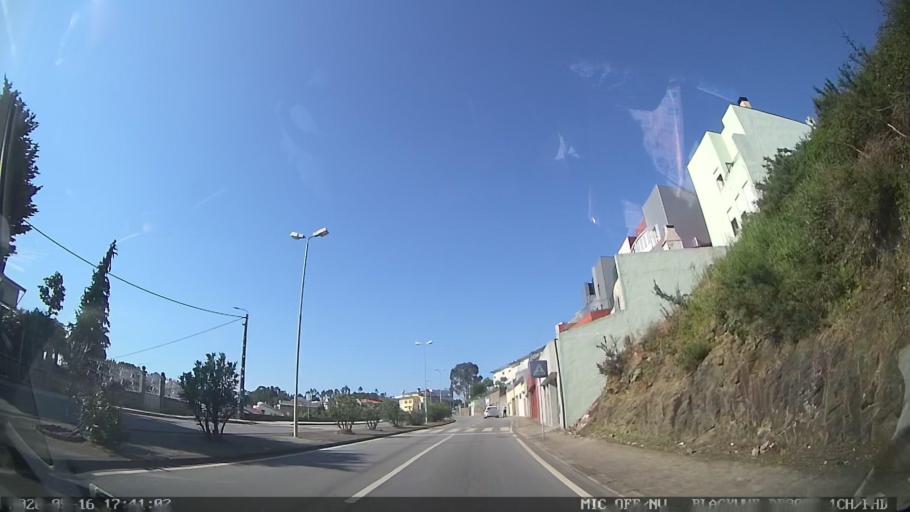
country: PT
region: Porto
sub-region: Valongo
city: Valongo
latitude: 41.1925
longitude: -8.5183
